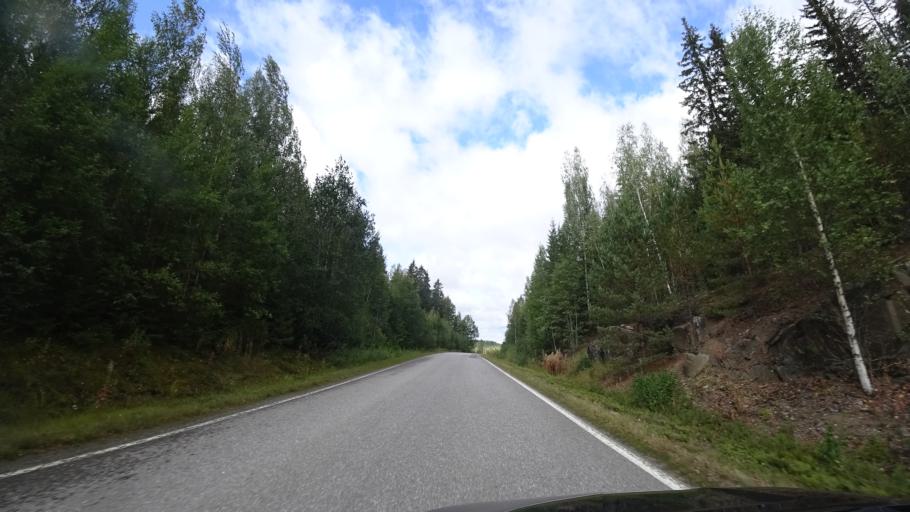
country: FI
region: Haeme
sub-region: Riihimaeki
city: Oitti
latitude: 60.8965
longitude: 25.0562
